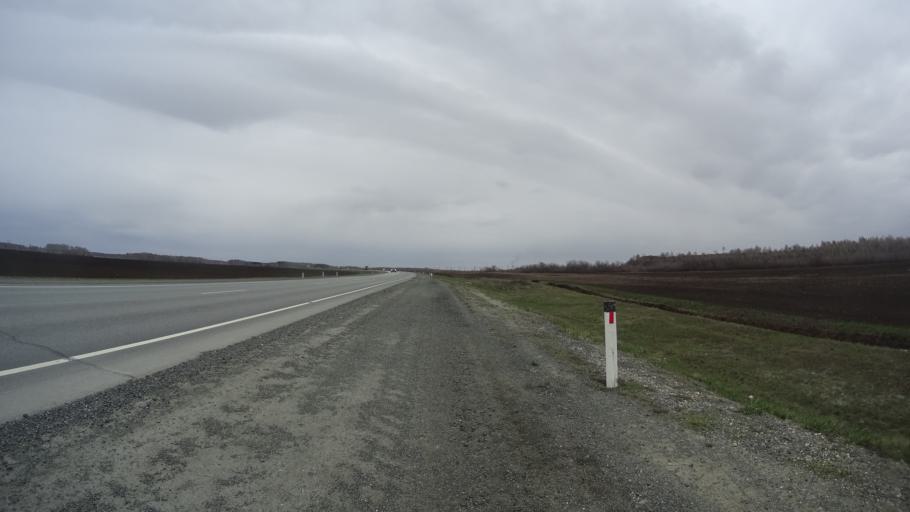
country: RU
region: Chelyabinsk
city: Krasnogorskiy
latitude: 54.5694
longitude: 61.2902
